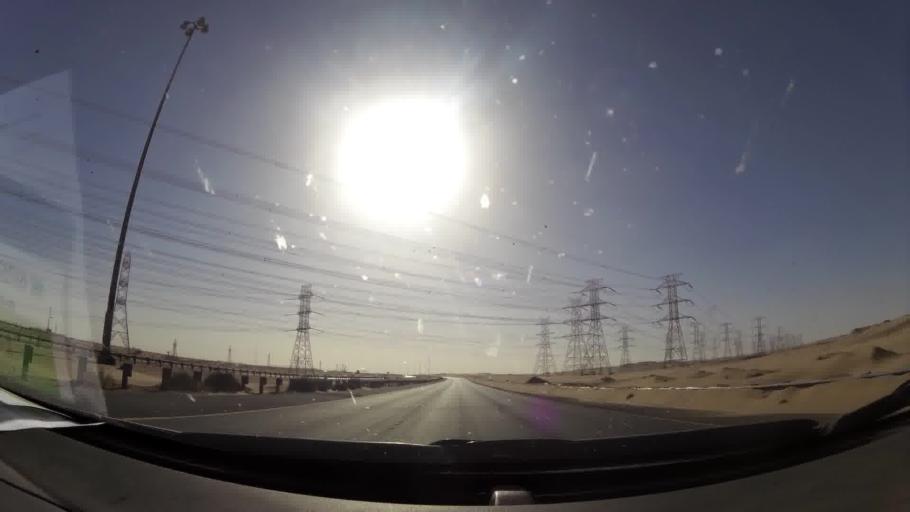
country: KW
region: Al Asimah
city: Kuwait City
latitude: 29.6273
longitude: 47.9250
